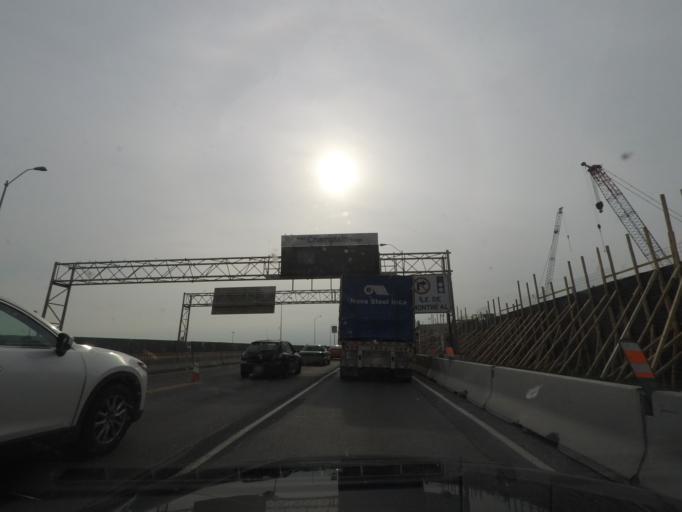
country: CA
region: Quebec
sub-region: Monteregie
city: Brossard
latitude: 45.4664
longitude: -73.4913
